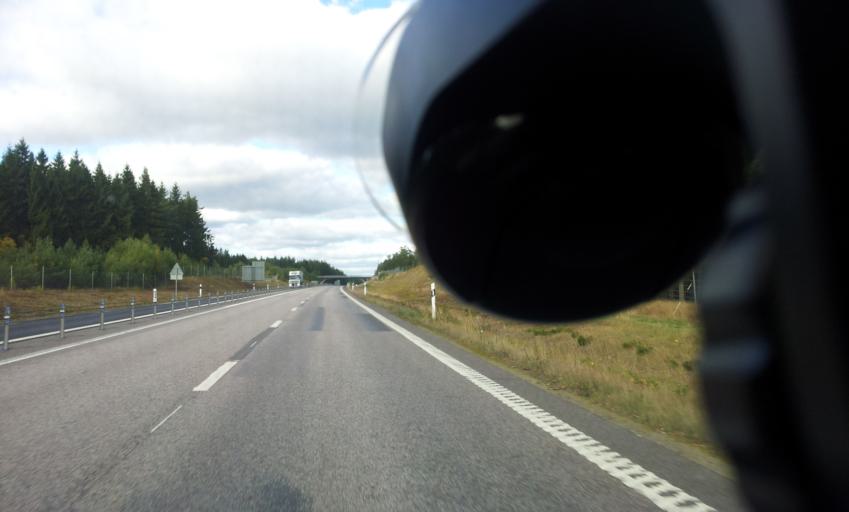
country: SE
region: Kalmar
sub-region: Torsas Kommun
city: Torsas
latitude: 56.4586
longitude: 16.0785
